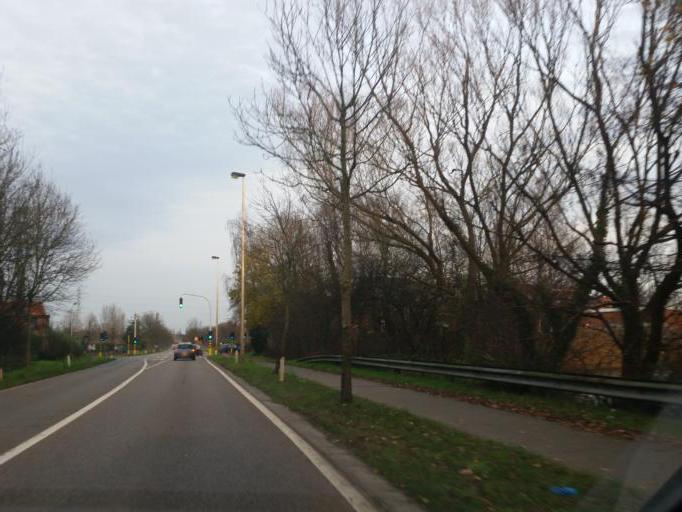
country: BE
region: Flanders
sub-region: Provincie Antwerpen
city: Duffel
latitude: 51.0928
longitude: 4.5191
